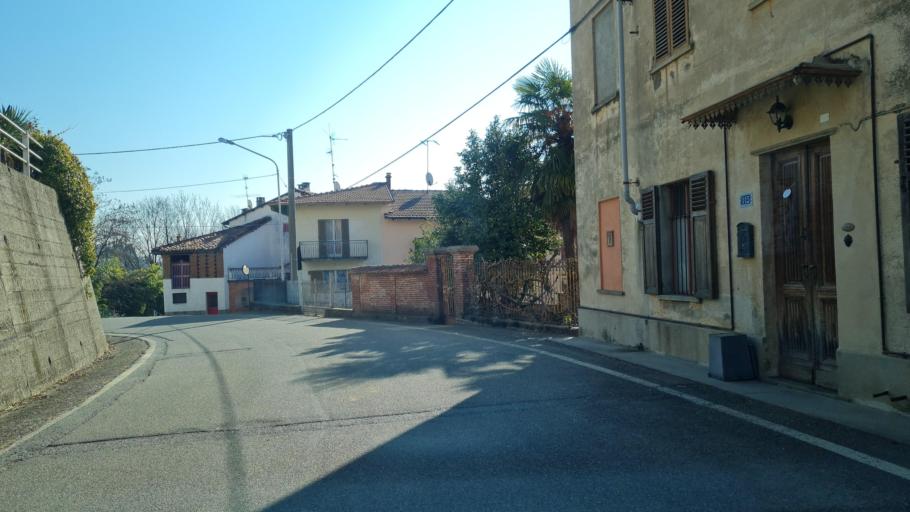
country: IT
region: Piedmont
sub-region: Provincia di Biella
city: Livera
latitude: 45.6121
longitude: 8.1164
